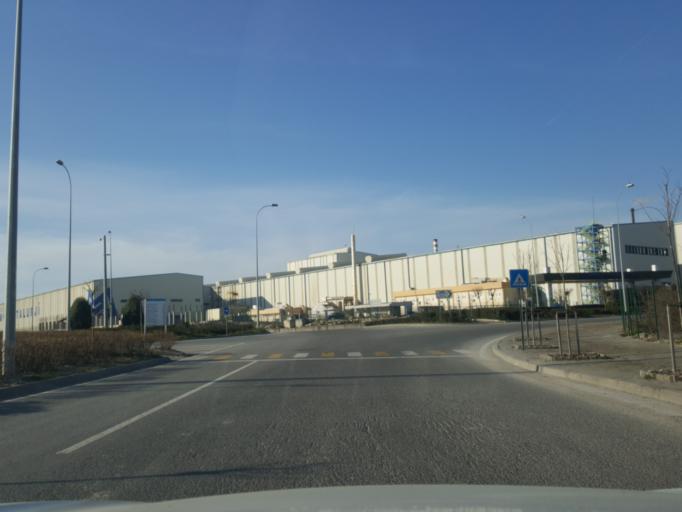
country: TR
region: Kocaeli
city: Tavsanli
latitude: 40.8303
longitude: 29.5585
